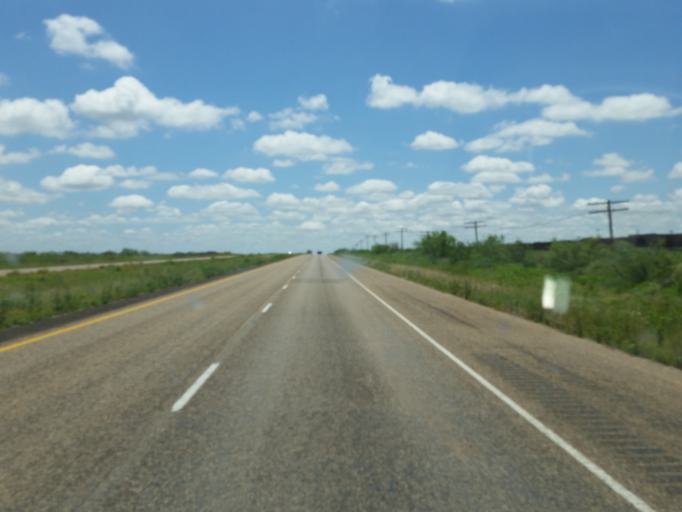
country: US
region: Texas
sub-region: Garza County
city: Post
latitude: 33.1321
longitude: -101.3026
